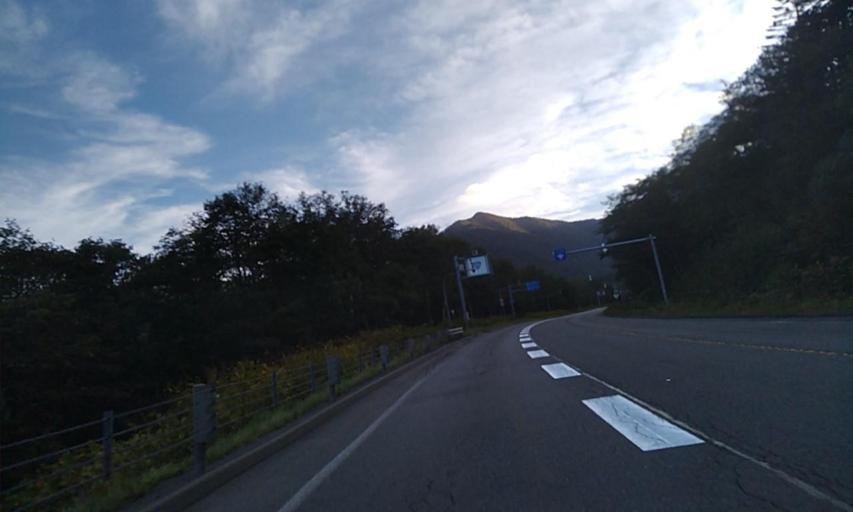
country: JP
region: Hokkaido
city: Otofuke
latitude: 42.9647
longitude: 142.7999
